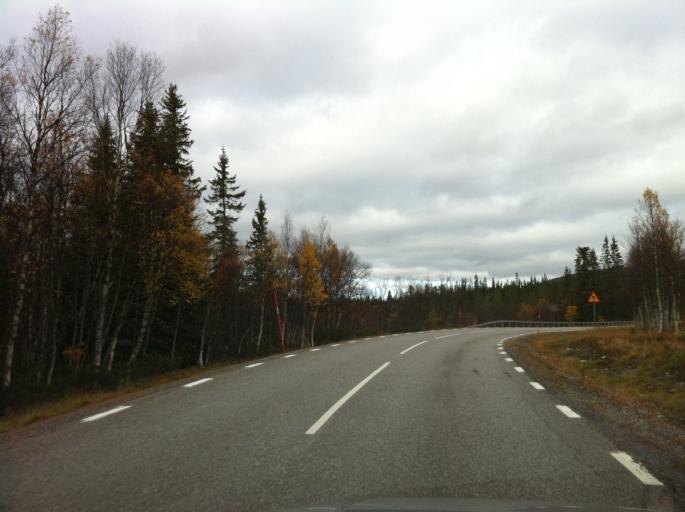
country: NO
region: Hedmark
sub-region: Engerdal
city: Engerdal
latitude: 62.0763
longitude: 12.3116
